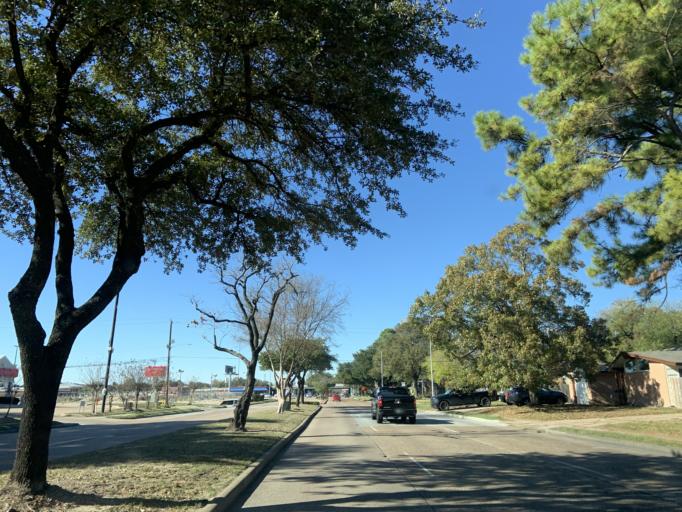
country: US
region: Texas
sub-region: Harris County
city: Bellaire
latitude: 29.6977
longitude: -95.5147
